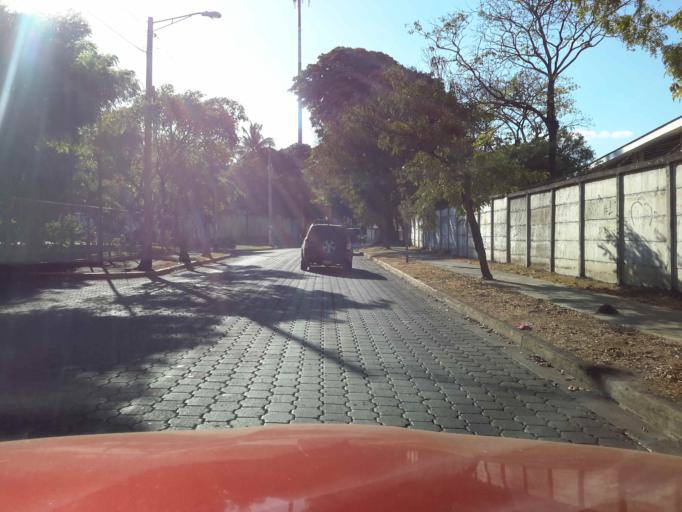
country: NI
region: Managua
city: Managua
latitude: 12.1296
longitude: -86.2956
